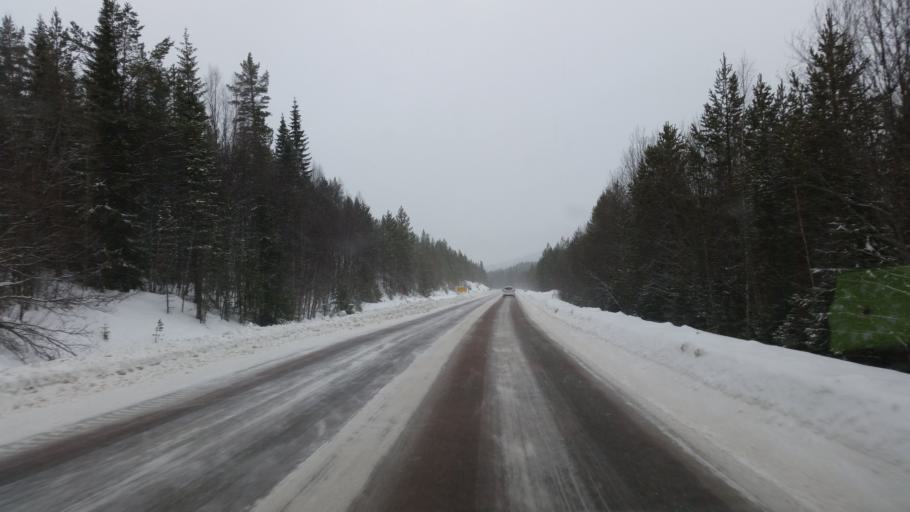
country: SE
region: Jaemtland
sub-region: Bergs Kommun
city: Hoverberg
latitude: 62.4897
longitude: 13.9222
